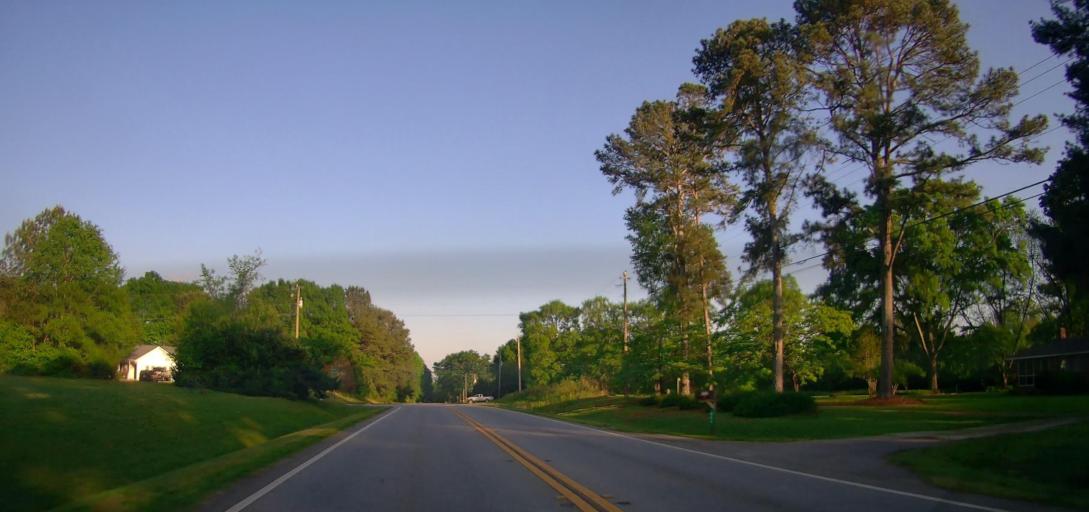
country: US
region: Georgia
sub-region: Newton County
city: Covington
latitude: 33.5754
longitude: -83.7725
